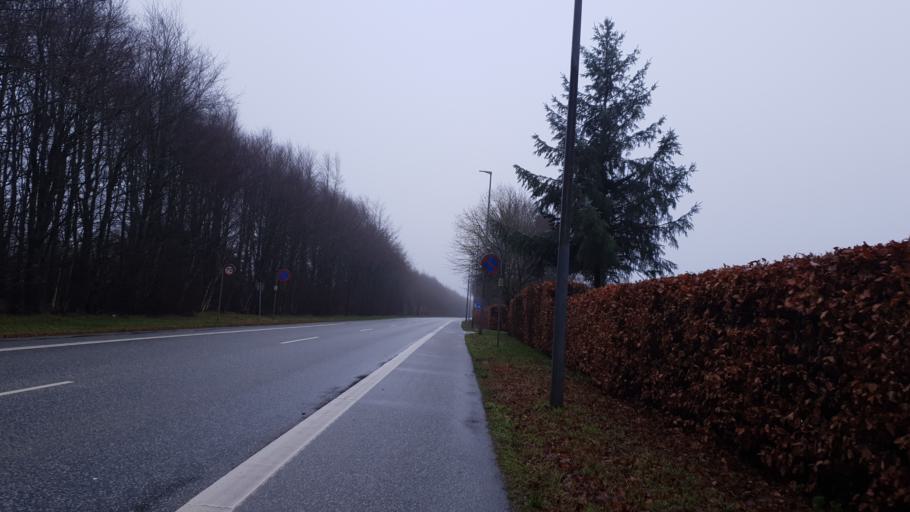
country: DK
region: Central Jutland
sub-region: Hedensted Kommune
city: Hedensted
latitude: 55.7927
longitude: 9.6996
